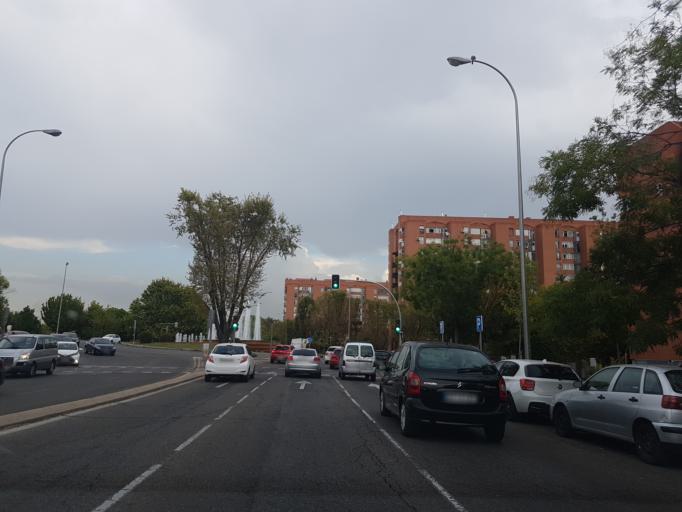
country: ES
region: Madrid
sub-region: Provincia de Madrid
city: Puente de Vallecas
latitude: 40.3940
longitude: -3.6413
